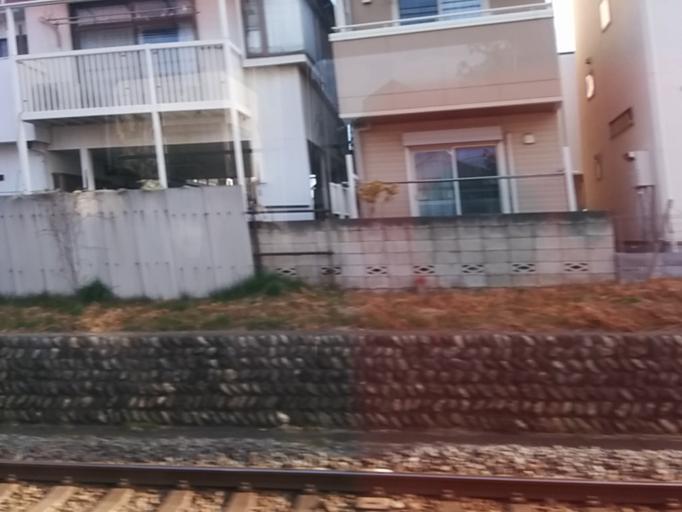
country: JP
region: Saitama
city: Kamifukuoka
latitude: 35.8771
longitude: 139.5091
